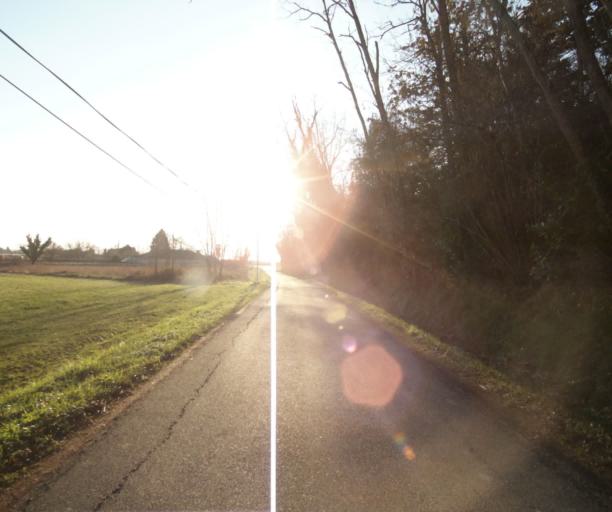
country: FR
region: Midi-Pyrenees
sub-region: Departement du Tarn-et-Garonne
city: Moissac
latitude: 44.1229
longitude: 1.1302
